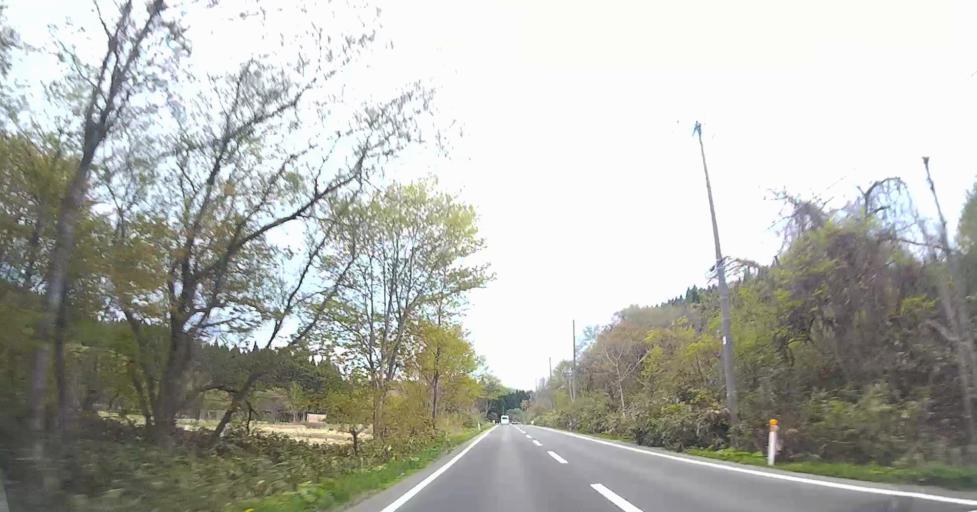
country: JP
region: Aomori
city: Goshogawara
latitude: 41.1231
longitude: 140.5211
